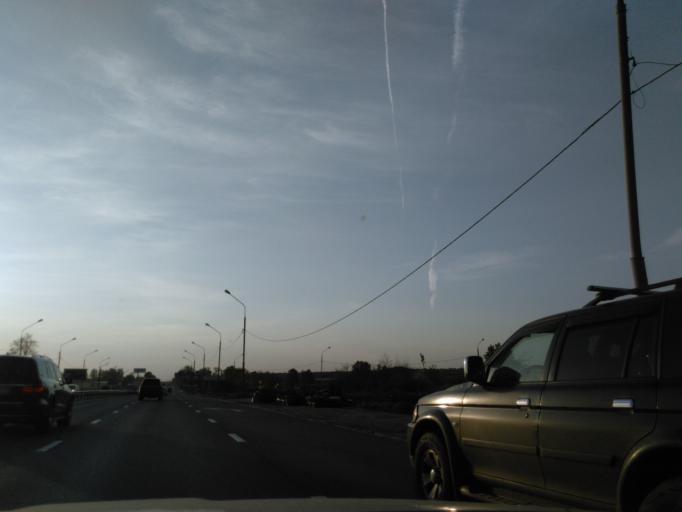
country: RU
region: Moskovskaya
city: Novopodrezkovo
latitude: 55.9553
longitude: 37.3436
